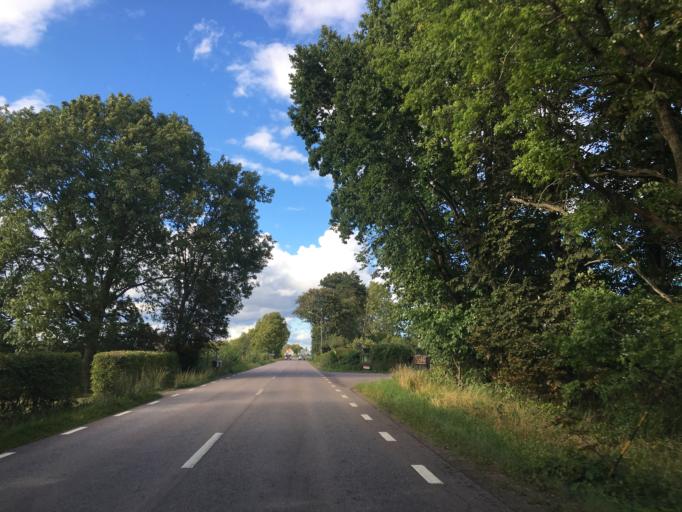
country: SE
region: Kalmar
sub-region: Morbylanga Kommun
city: Moerbylanga
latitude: 56.5130
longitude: 16.4382
